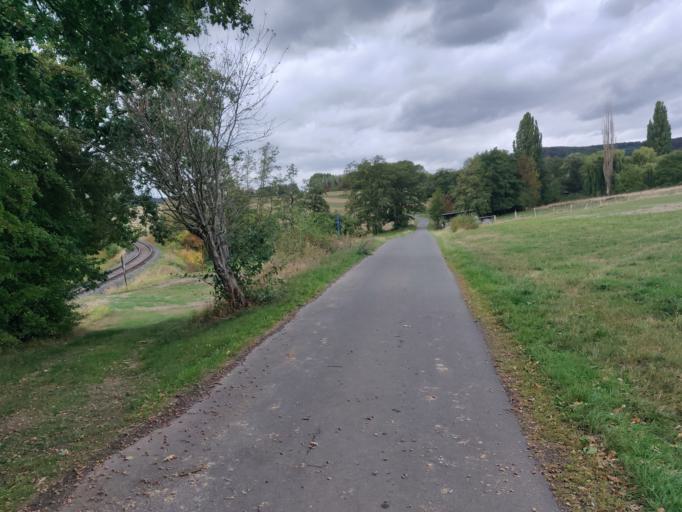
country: DE
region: Hesse
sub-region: Regierungsbezirk Kassel
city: Baunatal
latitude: 51.2833
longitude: 9.3621
